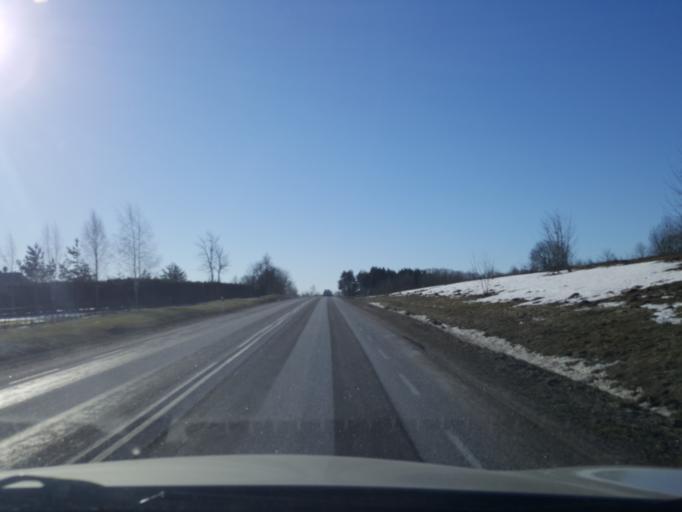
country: EE
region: Viljandimaa
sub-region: Viljandi linn
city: Viljandi
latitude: 58.3821
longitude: 25.6047
